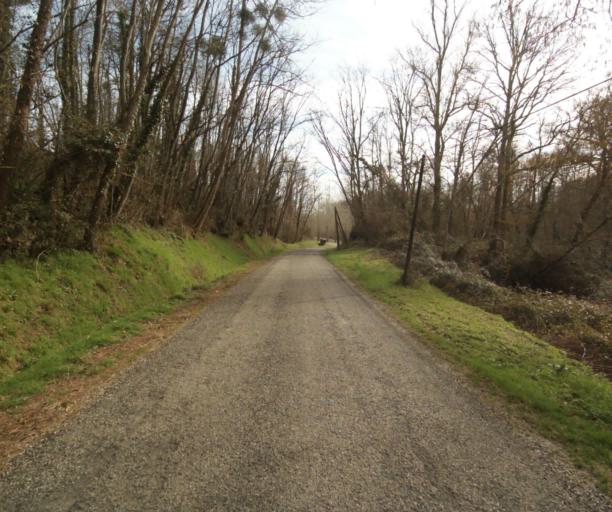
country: FR
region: Aquitaine
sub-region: Departement des Landes
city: Gabarret
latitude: 43.9790
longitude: 0.0263
